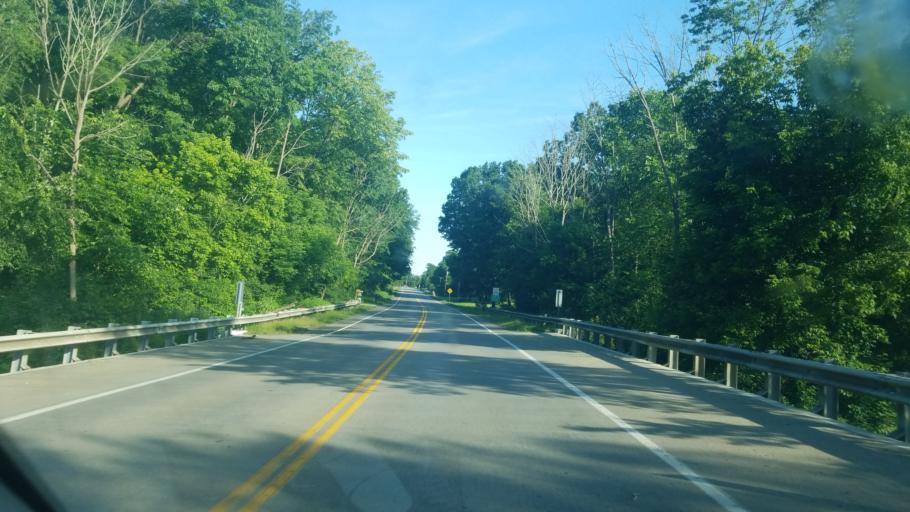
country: US
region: Ohio
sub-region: Columbiana County
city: Columbiana
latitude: 40.9054
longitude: -80.7012
